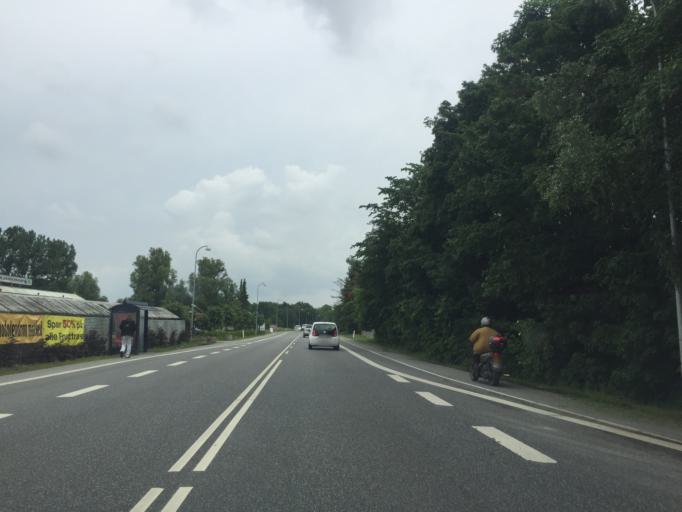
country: DK
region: Capital Region
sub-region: Fureso Kommune
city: Stavnsholt
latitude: 55.8202
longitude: 12.4139
